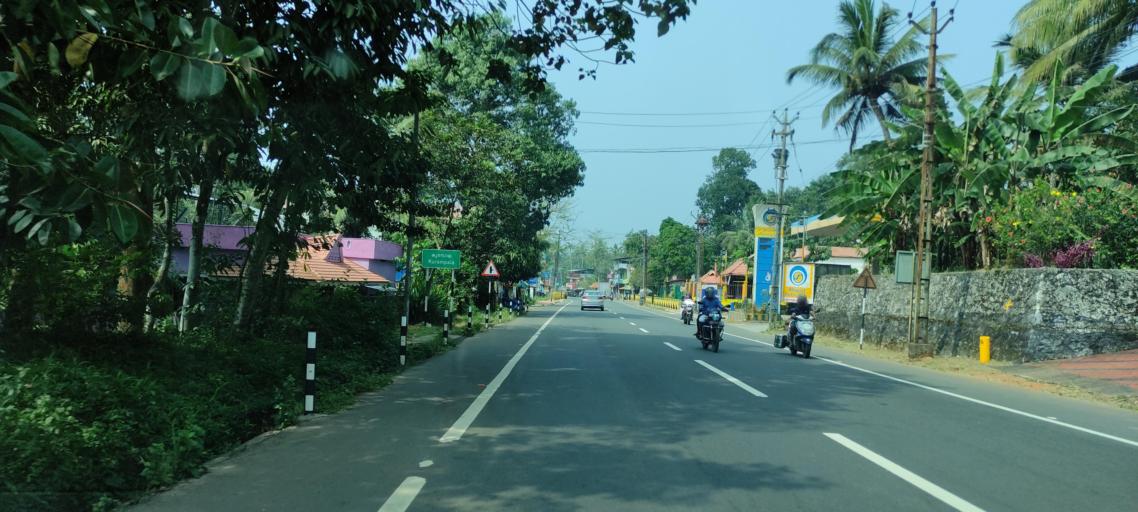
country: IN
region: Kerala
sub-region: Pattanamtitta
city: Adur
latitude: 9.1966
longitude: 76.6984
